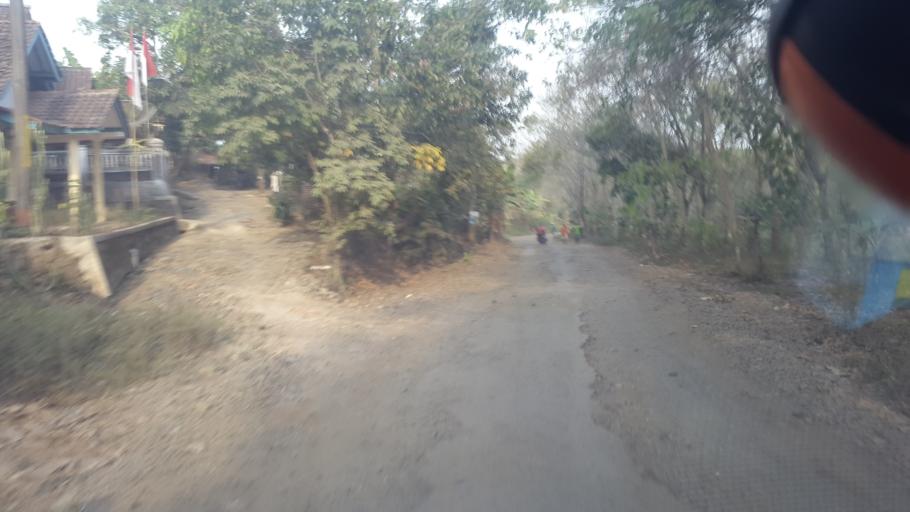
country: ID
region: West Java
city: Bojonggaling
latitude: -6.9555
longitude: 106.6329
